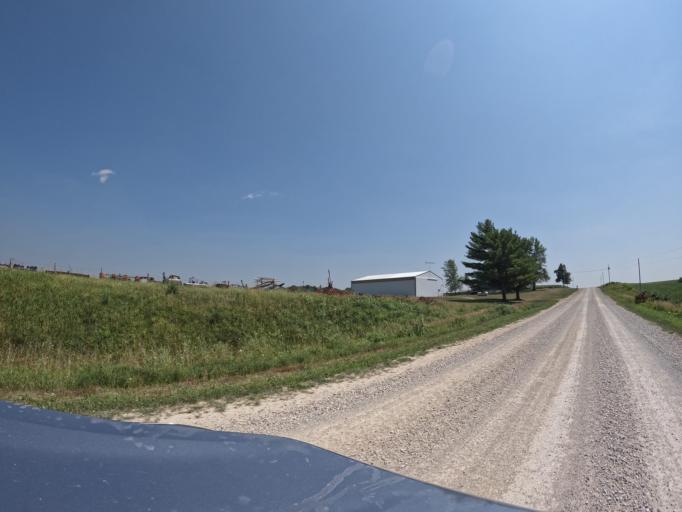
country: US
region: Iowa
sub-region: Keokuk County
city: Sigourney
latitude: 41.3452
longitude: -92.2388
